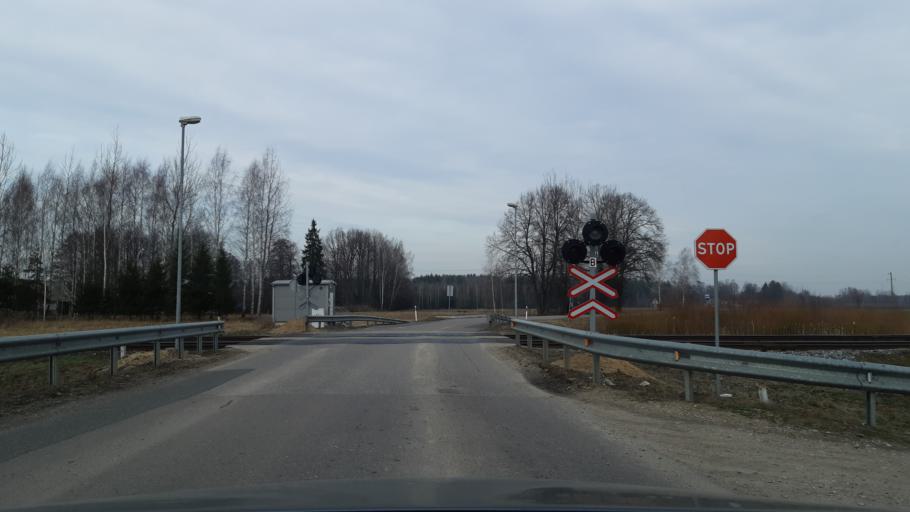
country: LT
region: Marijampoles apskritis
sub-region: Marijampole Municipality
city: Marijampole
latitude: 54.7269
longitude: 23.3362
